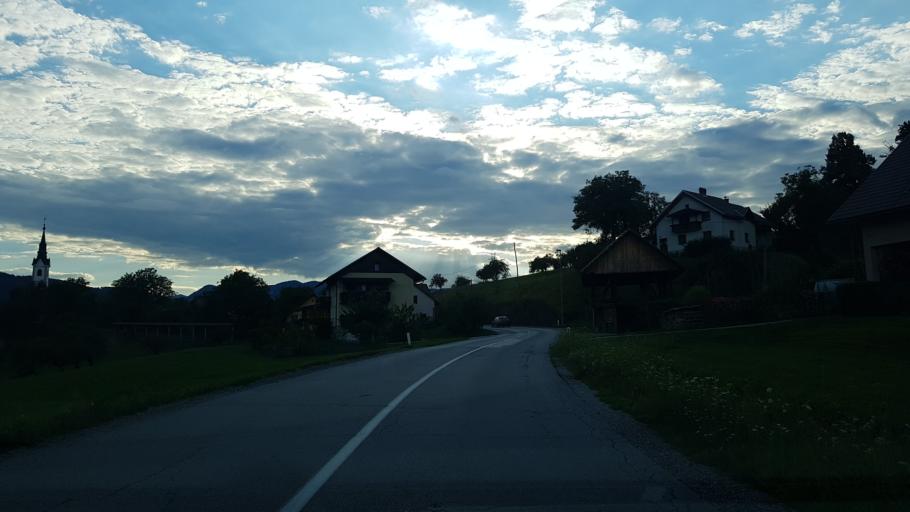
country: SI
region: Naklo
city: Naklo
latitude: 46.2580
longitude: 14.3103
